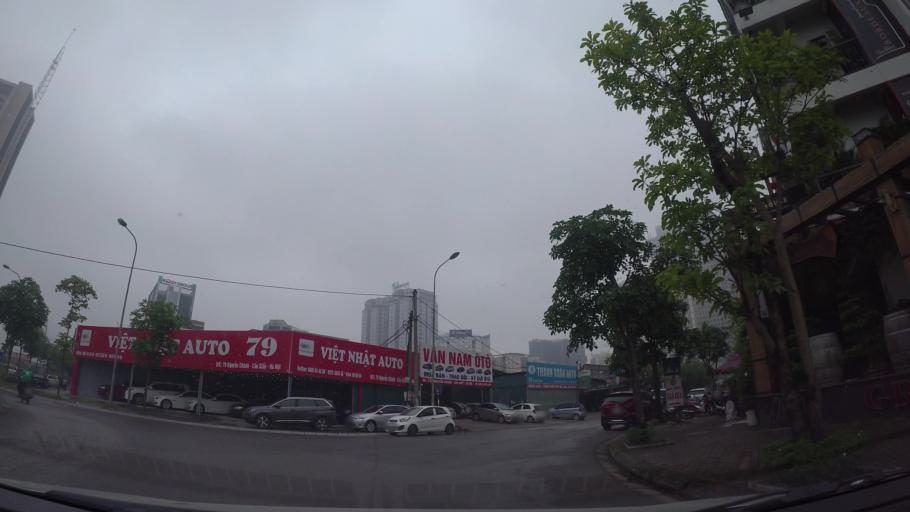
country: VN
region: Ha Noi
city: Cau Giay
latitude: 21.0192
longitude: 105.7867
